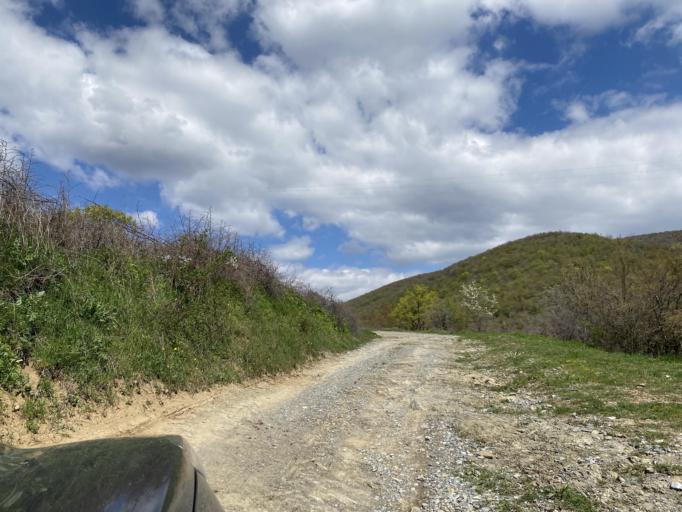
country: MK
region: Caska
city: Caska
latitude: 41.7350
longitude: 21.6477
